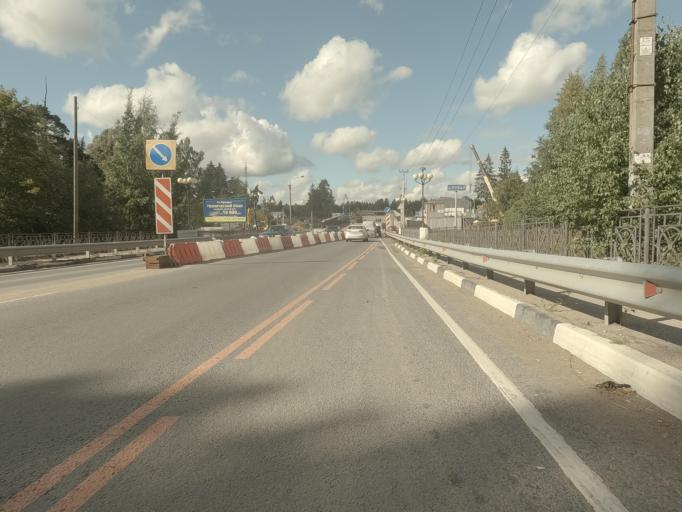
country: RU
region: Leningrad
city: Vsevolozhsk
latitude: 60.0127
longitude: 30.6663
